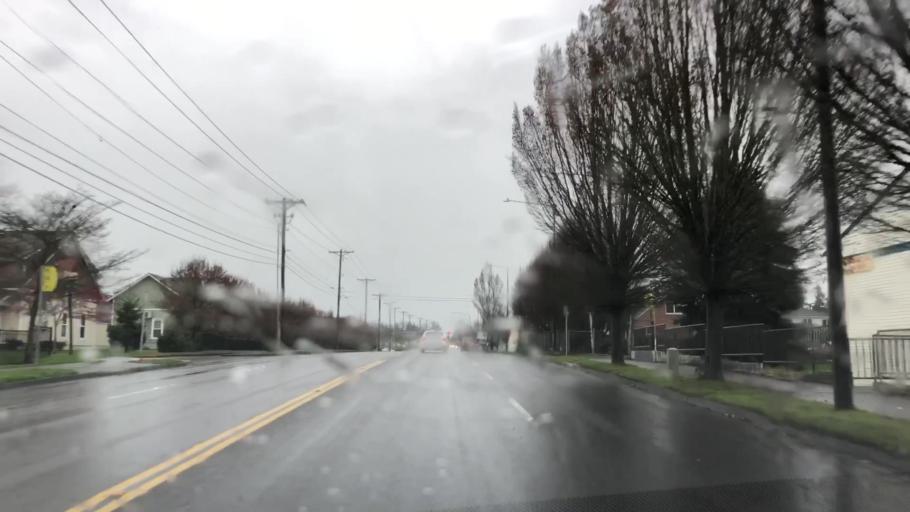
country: US
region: Washington
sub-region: Pierce County
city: Waller
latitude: 47.2160
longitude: -122.4077
